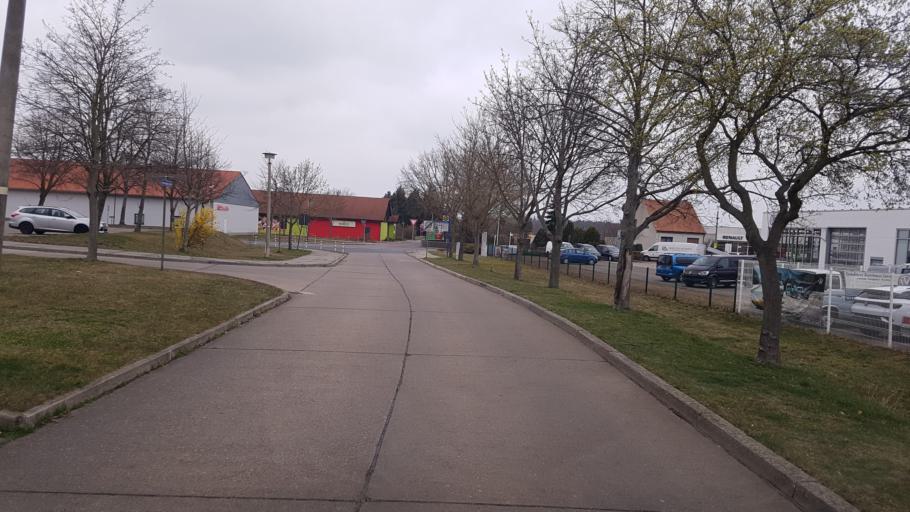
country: DE
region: Saxony
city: Nauwalde
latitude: 51.4180
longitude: 13.4576
